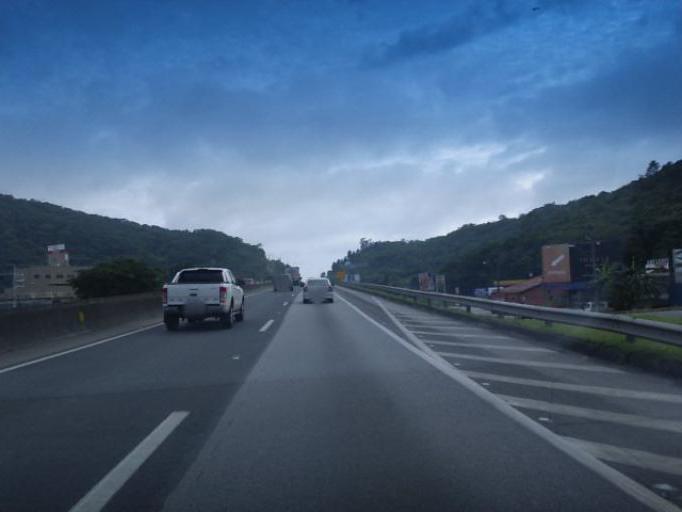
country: BR
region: Santa Catarina
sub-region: Itapema
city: Itapema
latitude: -27.0877
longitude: -48.6110
